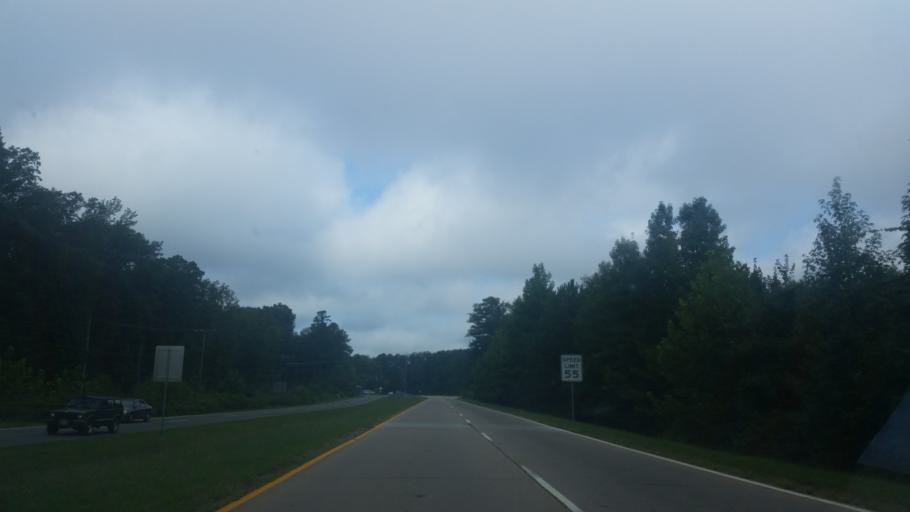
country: US
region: Virginia
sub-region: Henrico County
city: Sandston
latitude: 37.5123
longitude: -77.1950
